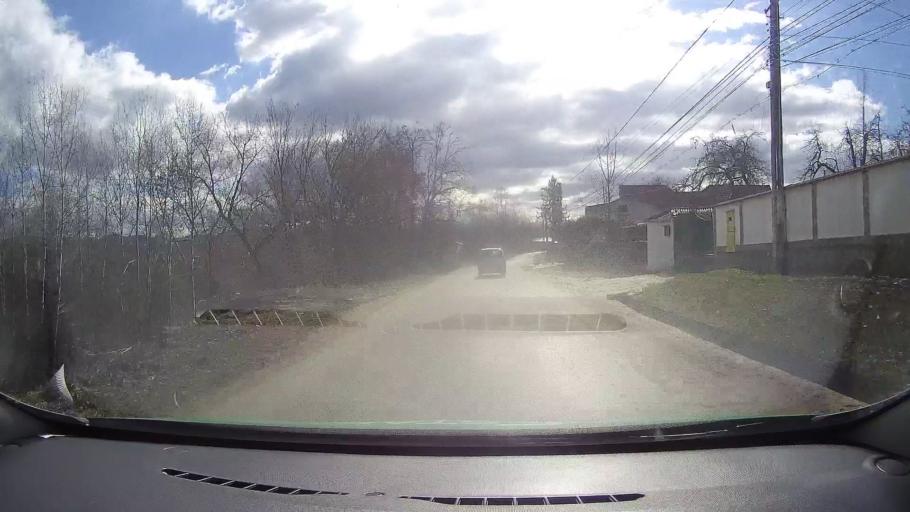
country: RO
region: Dambovita
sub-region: Oras Pucioasa
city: Pucioasa
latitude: 45.0651
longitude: 25.4245
